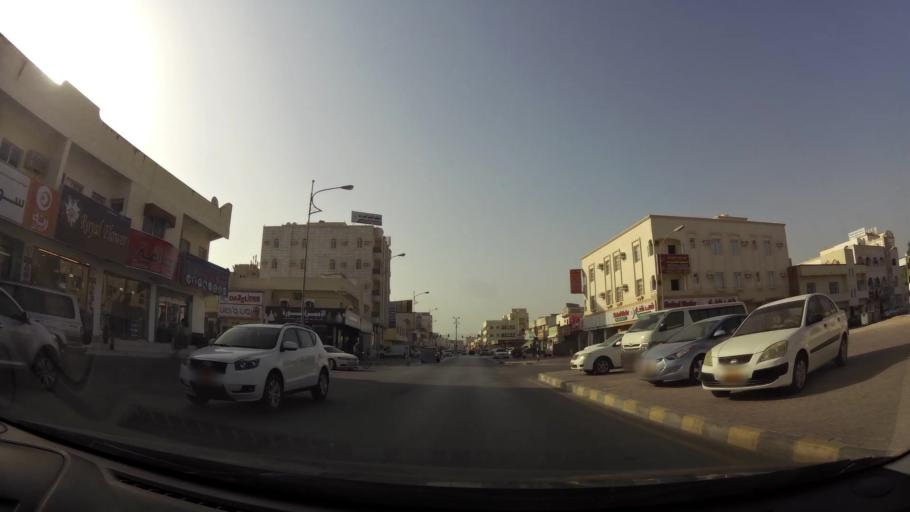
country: OM
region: Zufar
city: Salalah
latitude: 17.0117
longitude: 54.0860
